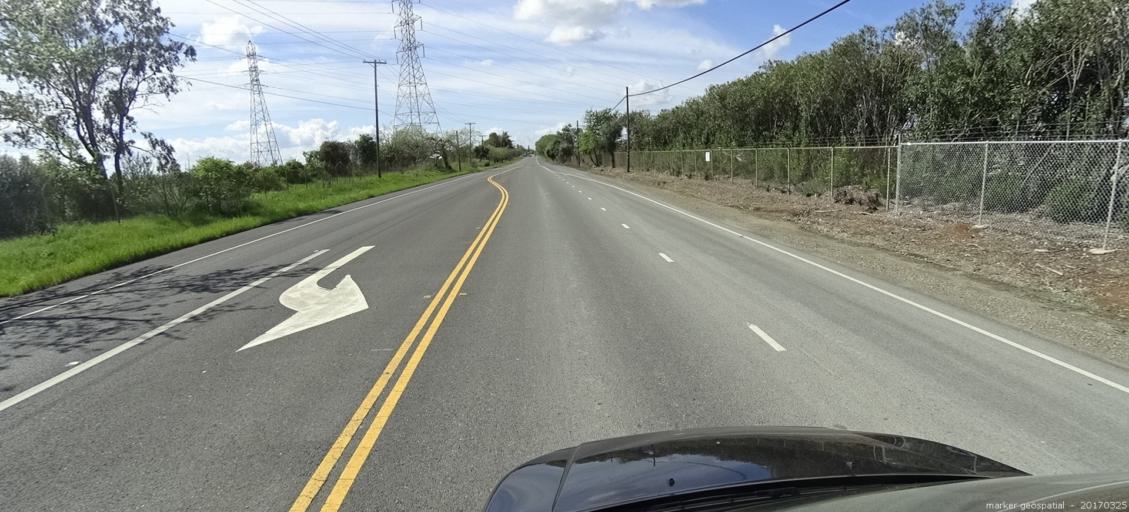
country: US
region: California
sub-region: Sacramento County
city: Rosemont
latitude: 38.5423
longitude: -121.3835
